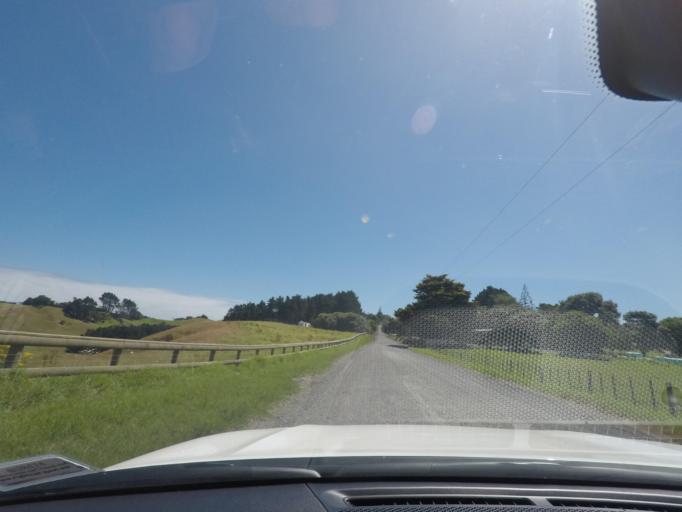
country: NZ
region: Auckland
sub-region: Auckland
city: Parakai
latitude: -36.5797
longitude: 174.3214
